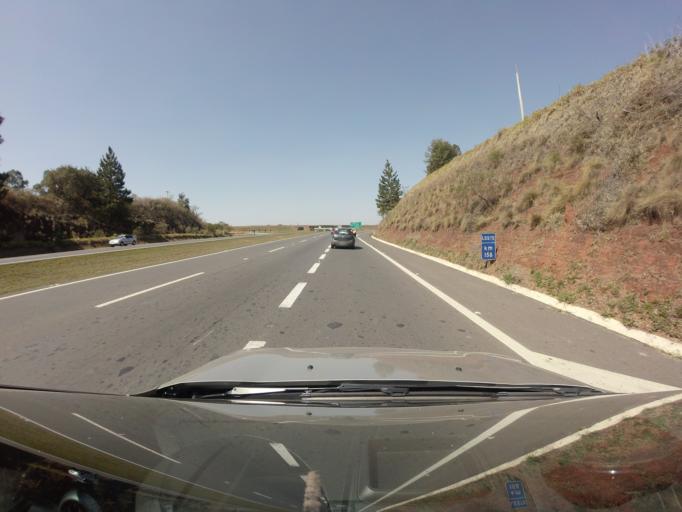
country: BR
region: Sao Paulo
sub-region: Piracicaba
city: Piracicaba
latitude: -22.7214
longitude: -47.6103
